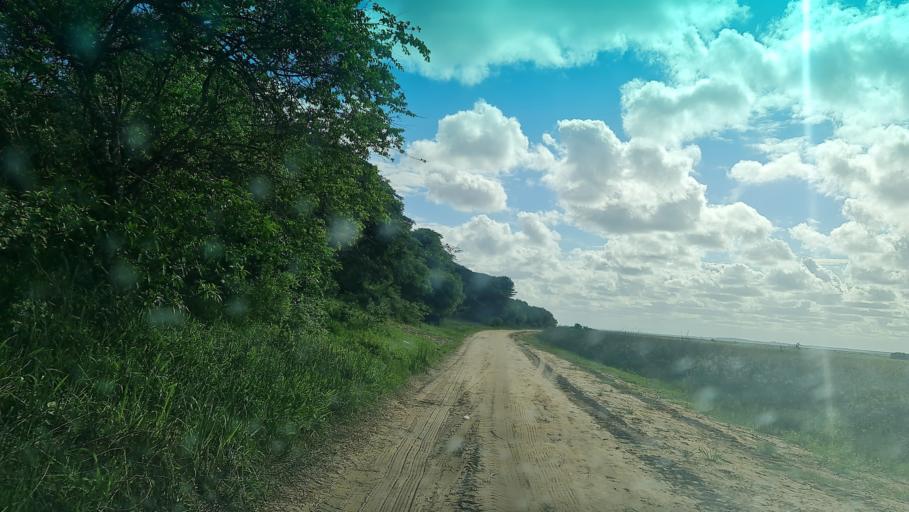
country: MZ
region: Maputo
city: Manhica
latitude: -25.4322
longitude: 32.8899
